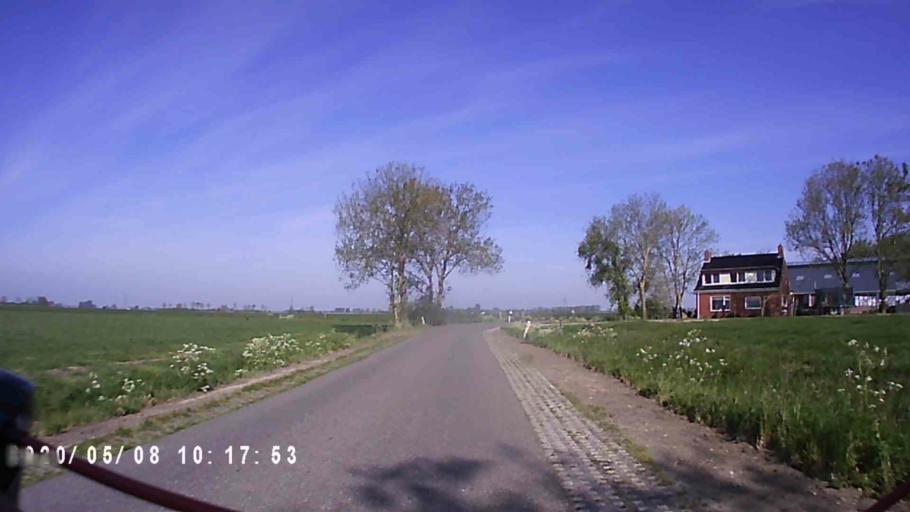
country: NL
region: Groningen
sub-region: Gemeente Winsum
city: Winsum
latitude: 53.2931
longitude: 6.4935
